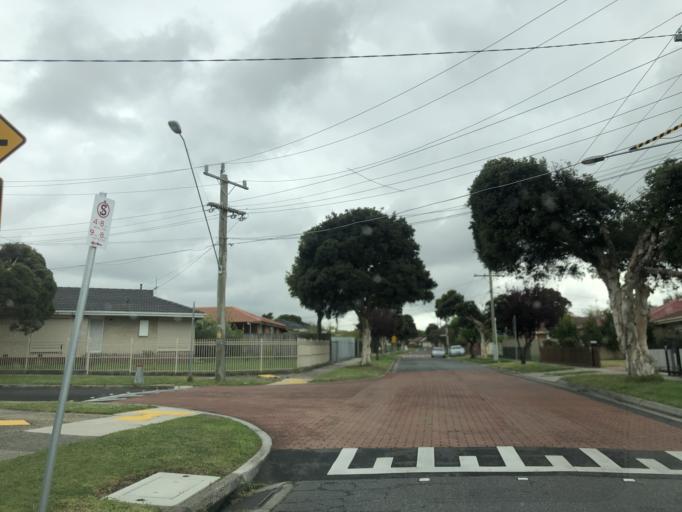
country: AU
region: Victoria
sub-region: Greater Dandenong
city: Dandenong North
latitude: -37.9628
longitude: 145.2152
